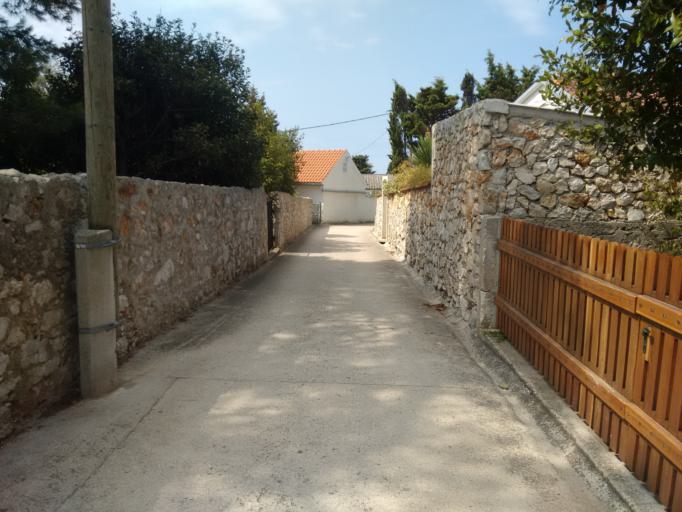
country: HR
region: Licko-Senjska
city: Novalja
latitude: 44.3749
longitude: 14.6946
